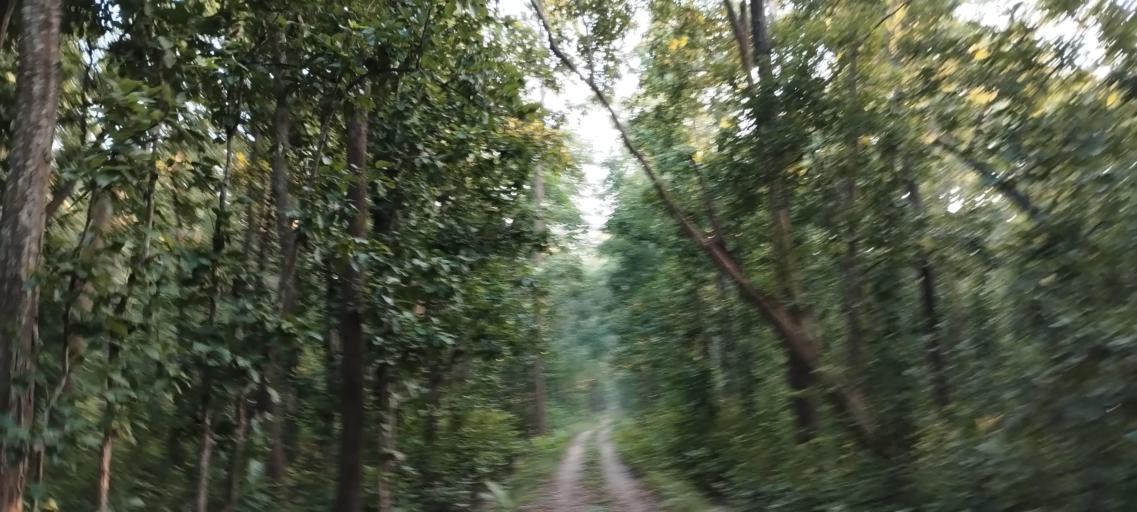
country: NP
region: Far Western
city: Tikapur
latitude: 28.4901
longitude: 81.2654
